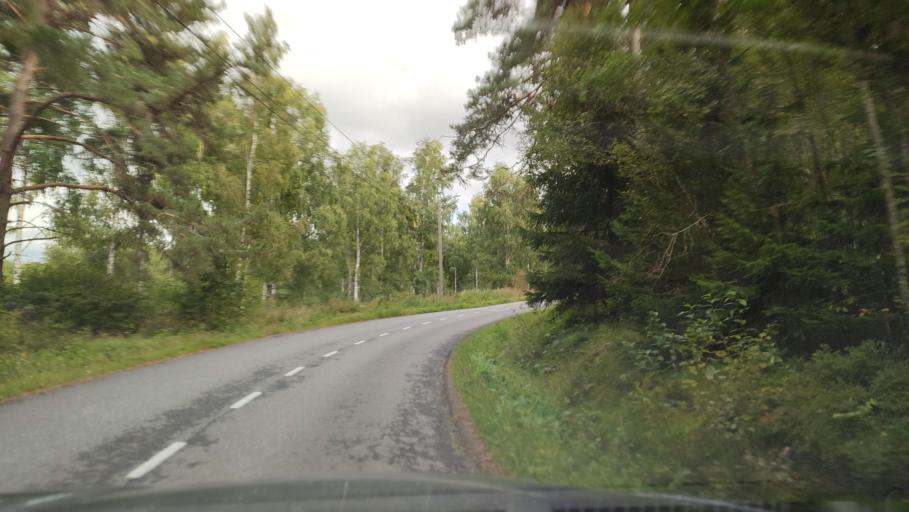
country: FI
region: Ostrobothnia
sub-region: Sydosterbotten
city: Kristinestad
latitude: 62.2764
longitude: 21.3542
